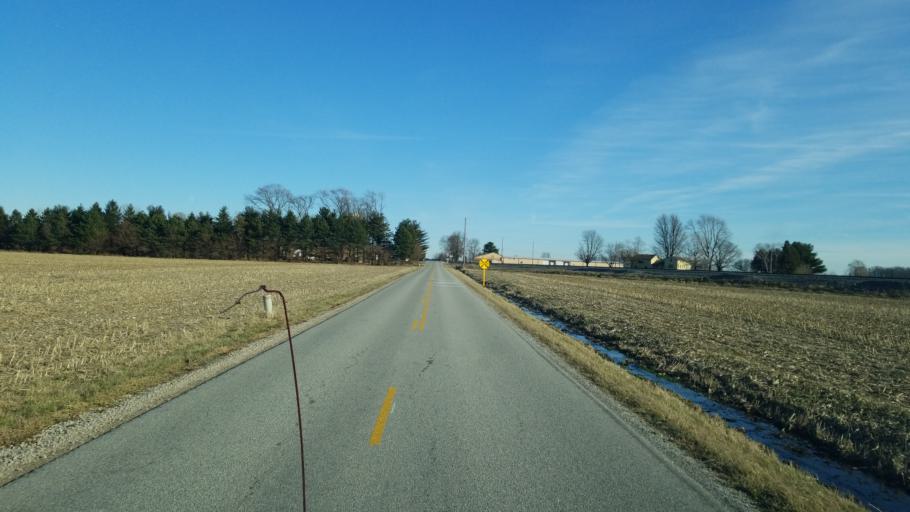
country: US
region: Ohio
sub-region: Sandusky County
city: Green Springs
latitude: 41.2560
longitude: -83.0167
